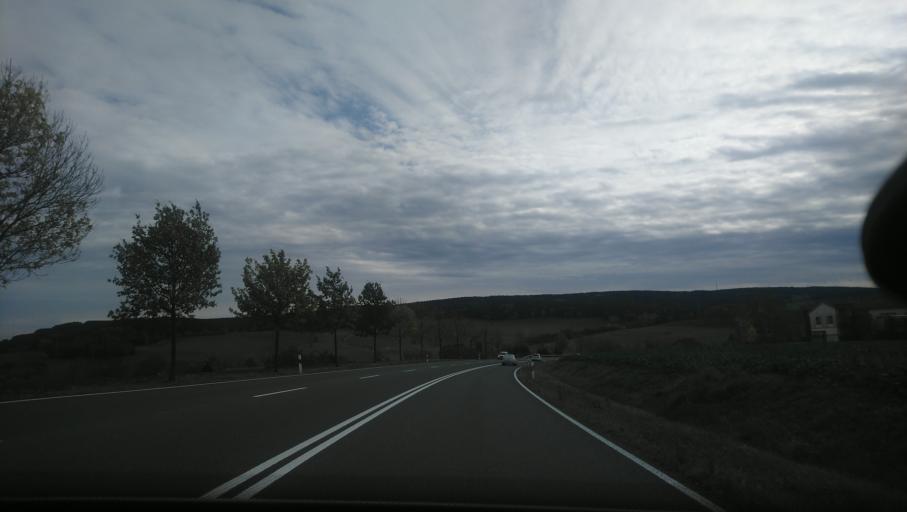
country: DE
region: Saxony
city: Dorfchemnitz
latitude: 50.6516
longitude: 12.8217
